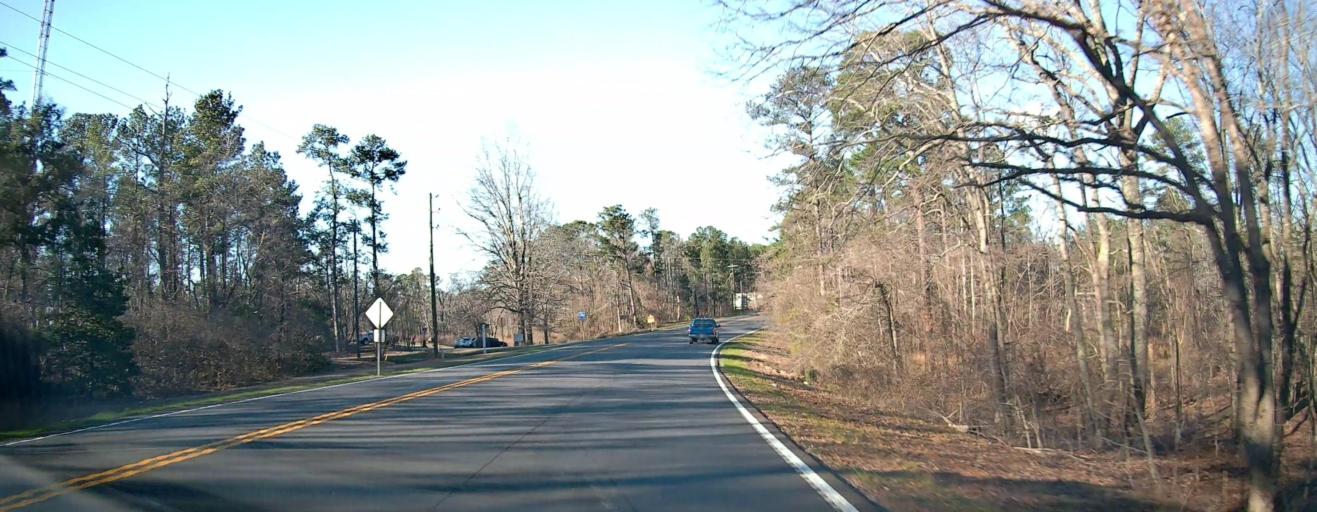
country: US
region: Georgia
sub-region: Meriwether County
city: Manchester
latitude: 32.8509
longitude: -84.7002
